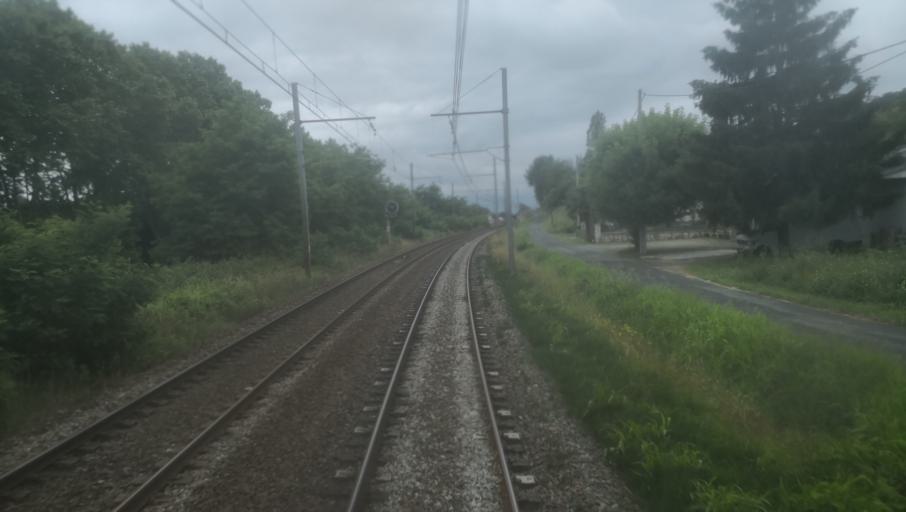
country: FR
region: Aquitaine
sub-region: Departement du Lot-et-Garonne
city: Colayrac-Saint-Cirq
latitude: 44.2410
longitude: 0.4866
